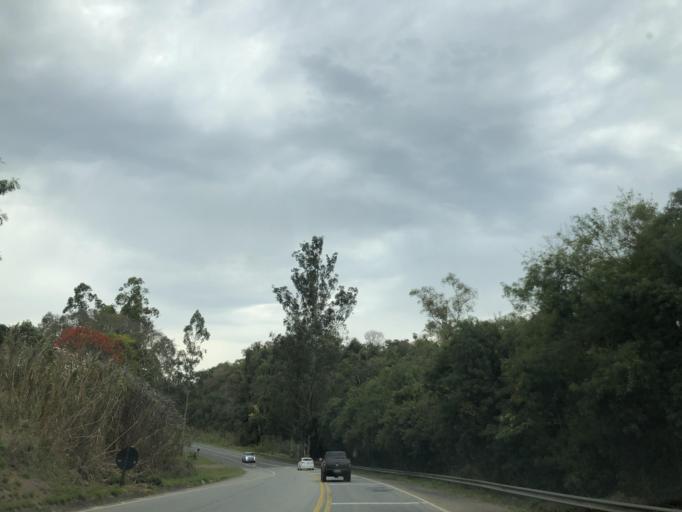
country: BR
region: Sao Paulo
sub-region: Salto De Pirapora
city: Salto de Pirapora
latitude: -23.7328
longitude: -47.6392
